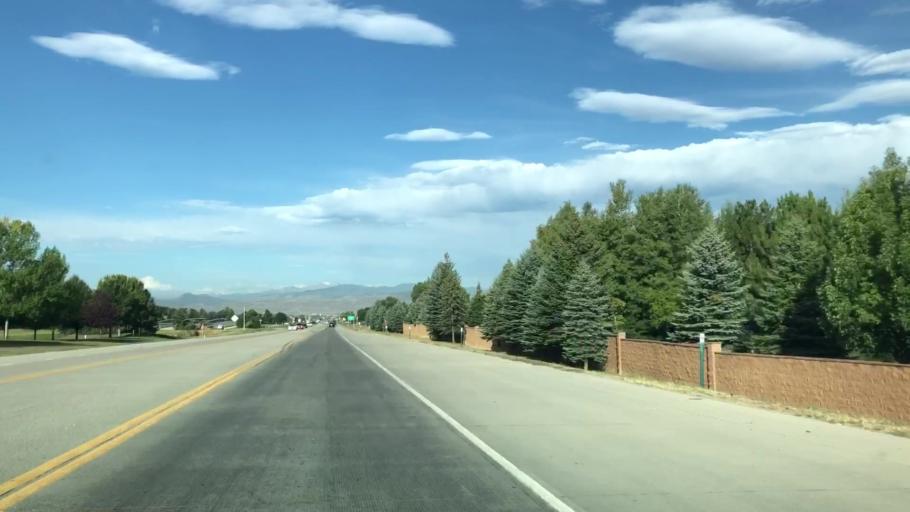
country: US
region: Colorado
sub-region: Weld County
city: Windsor
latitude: 40.4796
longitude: -104.9751
